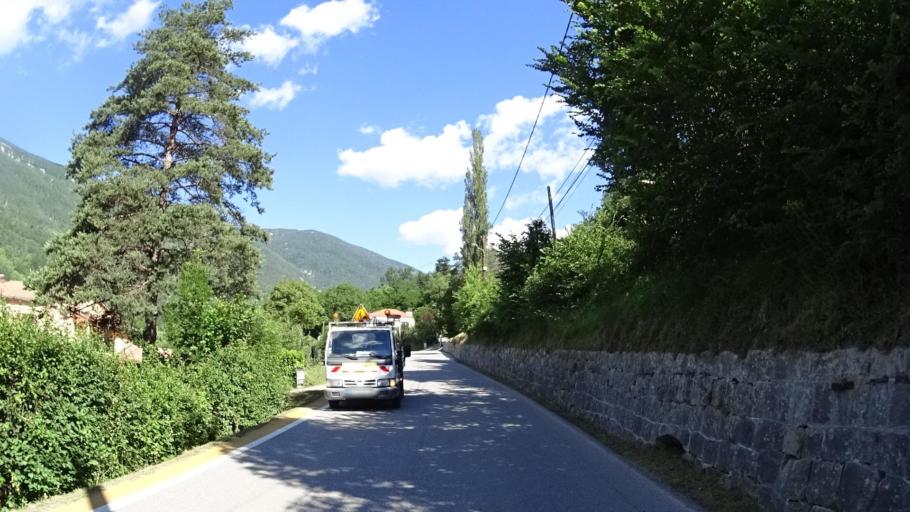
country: FR
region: Provence-Alpes-Cote d'Azur
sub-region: Departement des Alpes-de-Haute-Provence
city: Annot
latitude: 43.9705
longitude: 6.6609
